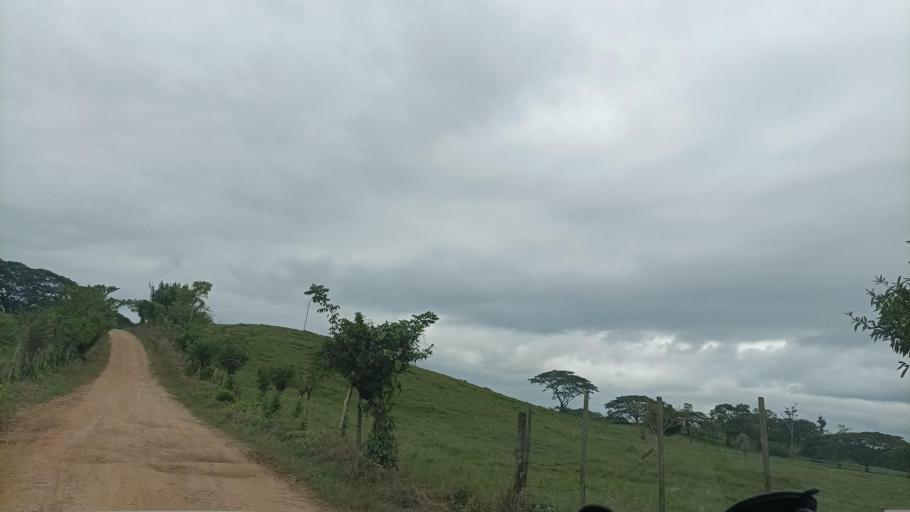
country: MX
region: Veracruz
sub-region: Uxpanapa
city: Poblado Cinco
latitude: 17.4960
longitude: -94.5658
